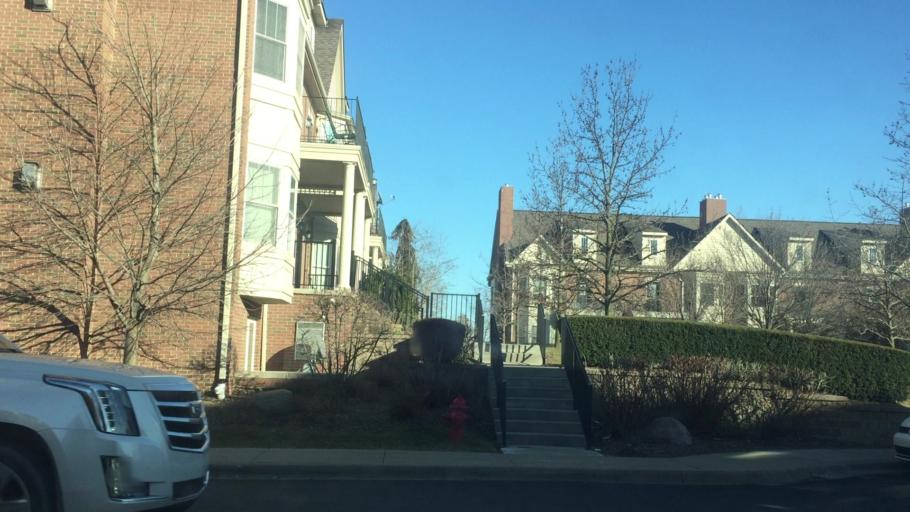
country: US
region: Michigan
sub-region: Oakland County
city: Novi
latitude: 42.4784
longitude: -83.4596
